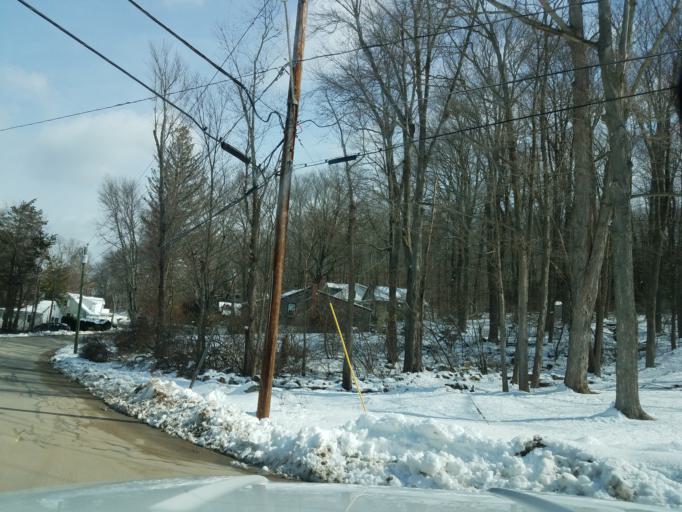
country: US
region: Connecticut
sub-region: Tolland County
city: Hebron
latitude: 41.7128
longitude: -72.3543
